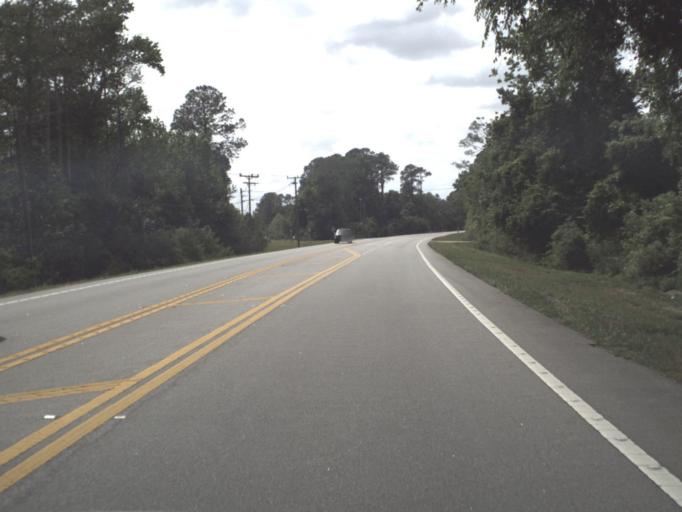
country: US
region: Florida
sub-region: Flagler County
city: Bunnell
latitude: 29.4684
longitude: -81.3125
